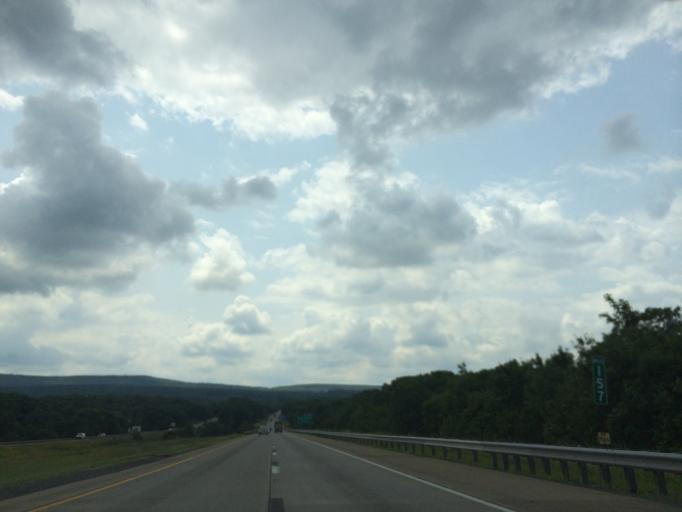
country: US
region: Pennsylvania
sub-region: Luzerne County
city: Nanticoke
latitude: 41.1161
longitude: -75.9619
